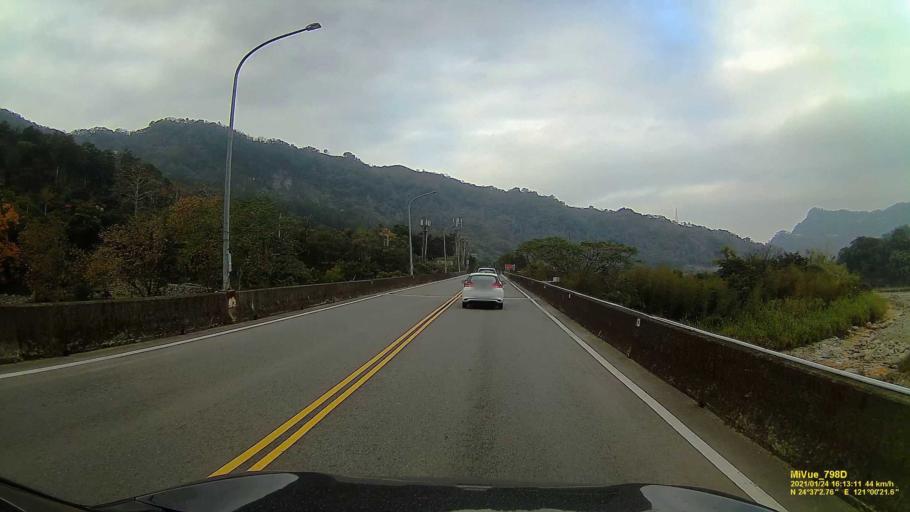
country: TW
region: Taiwan
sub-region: Hsinchu
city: Hsinchu
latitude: 24.6176
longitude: 121.0059
